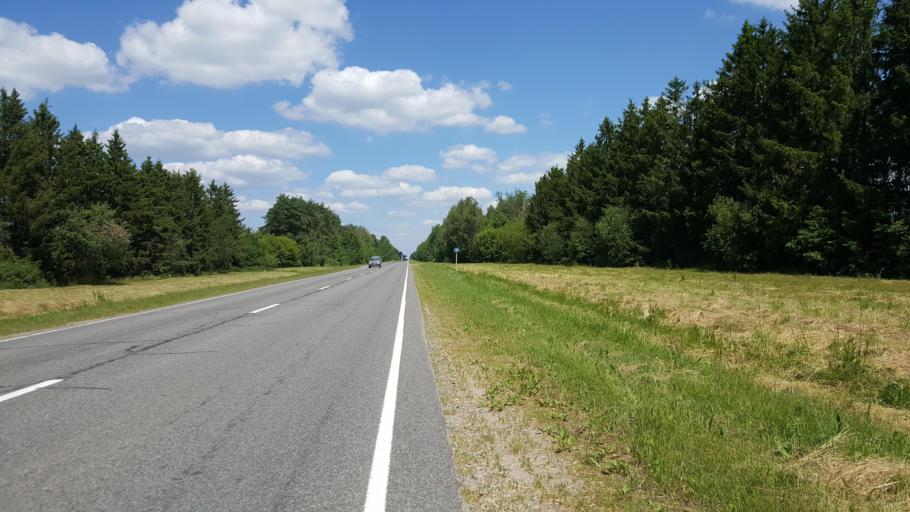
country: BY
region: Brest
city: Kamyanyets
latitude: 52.4349
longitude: 23.7856
